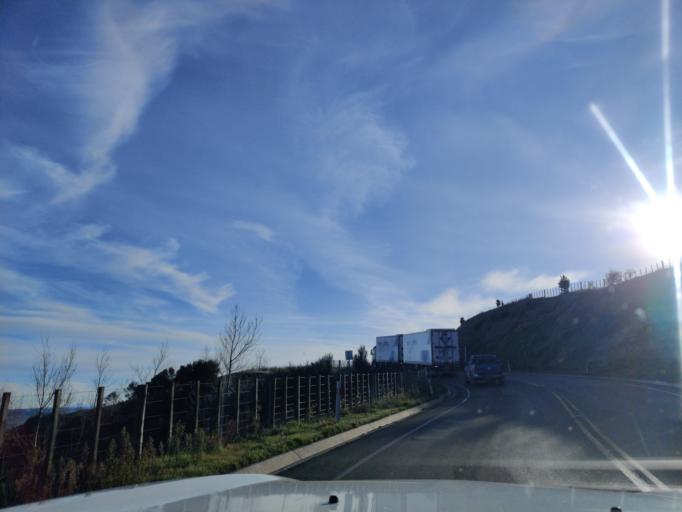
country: NZ
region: Manawatu-Wanganui
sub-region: Palmerston North City
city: Palmerston North
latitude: -40.2875
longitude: 175.7865
